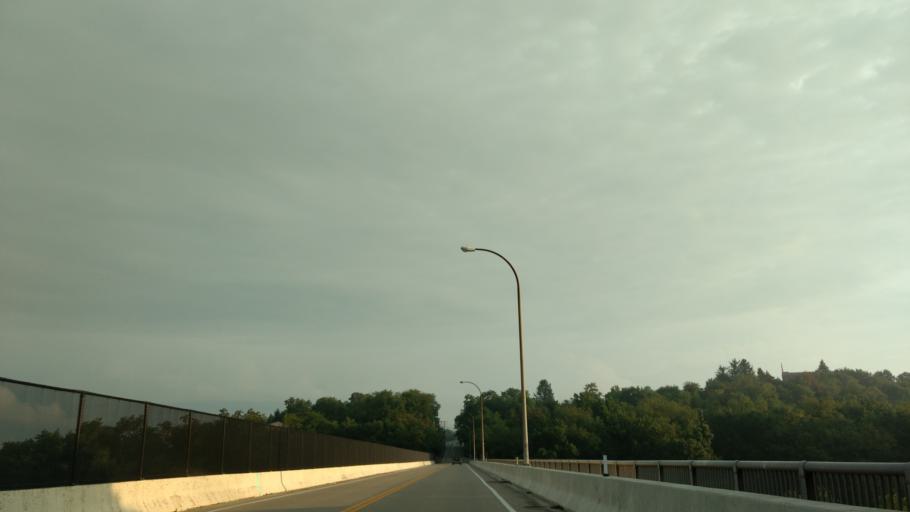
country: US
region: Pennsylvania
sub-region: Allegheny County
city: West View
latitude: 40.5103
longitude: -80.0459
